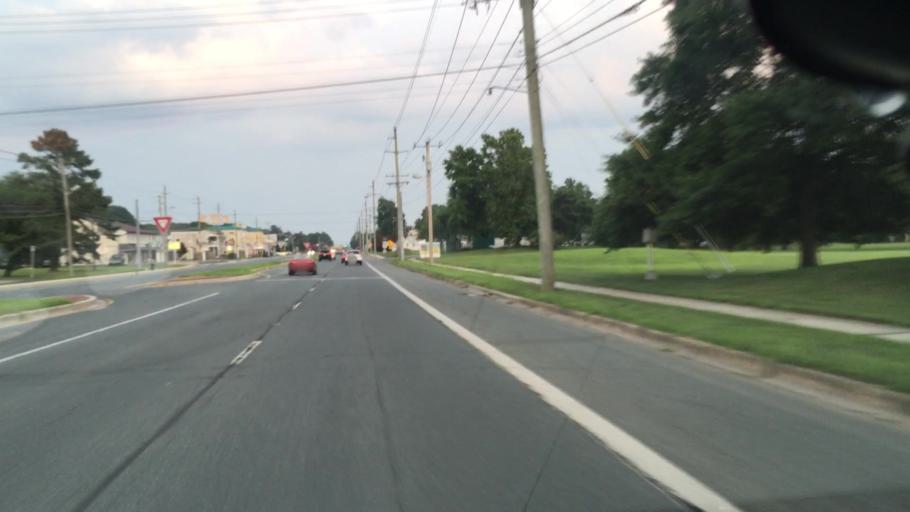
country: US
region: Delaware
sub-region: Sussex County
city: Rehoboth Beach
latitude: 38.7045
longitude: -75.0858
